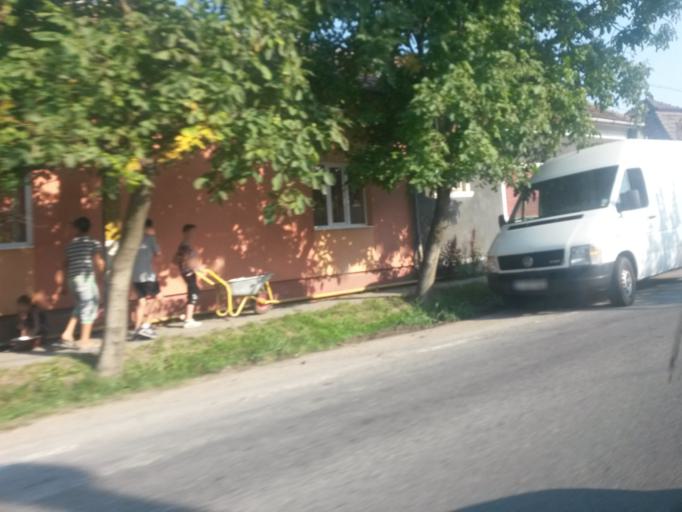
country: RO
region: Alba
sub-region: Comuna Unirea
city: Unirea
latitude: 46.3996
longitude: 23.8093
